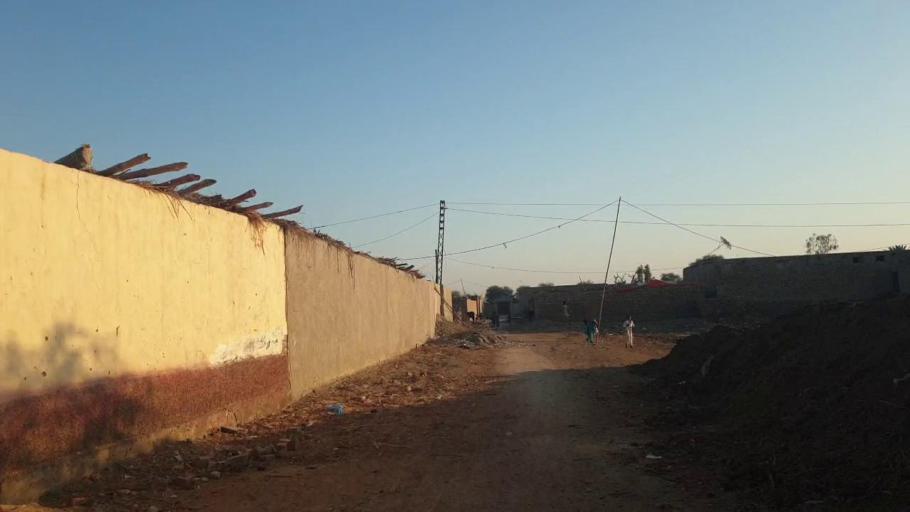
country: PK
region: Sindh
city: Khadro
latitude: 26.0737
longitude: 68.6916
